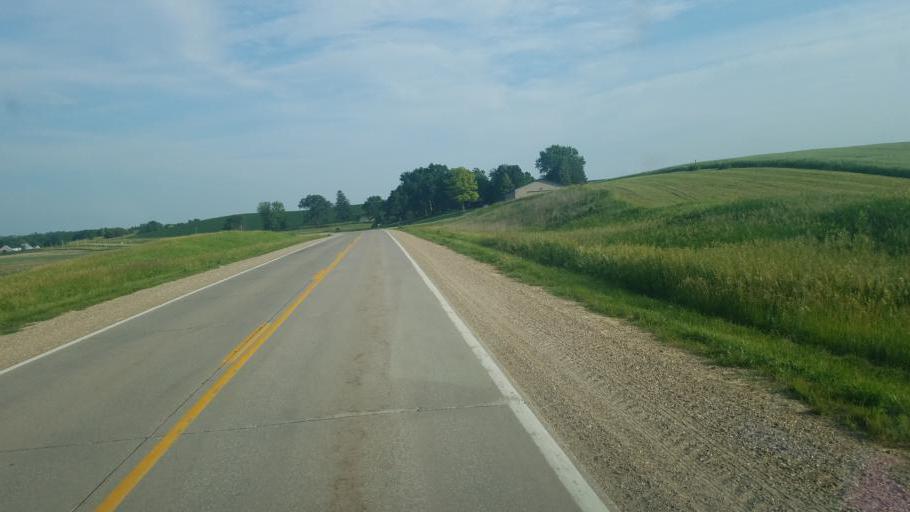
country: US
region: Iowa
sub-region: Tama County
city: Toledo
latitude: 41.9930
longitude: -92.7257
